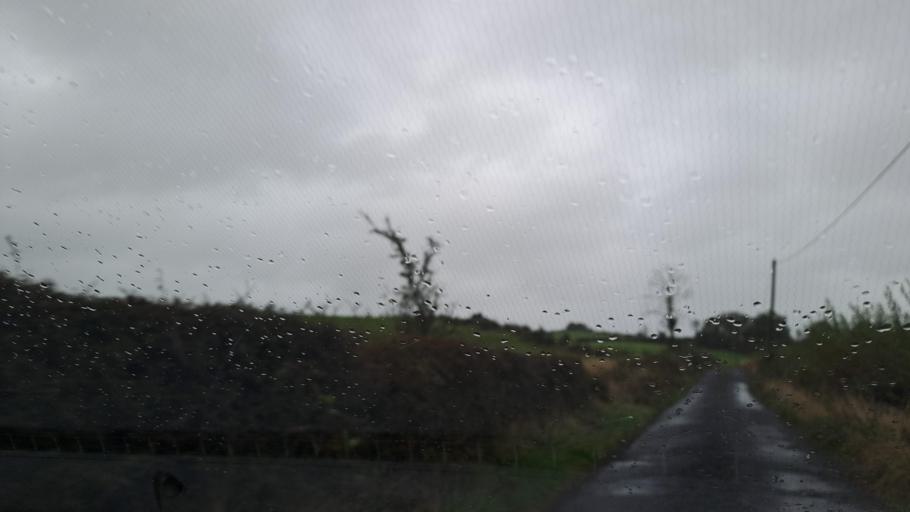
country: IE
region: Ulster
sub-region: An Cabhan
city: Kingscourt
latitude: 54.0069
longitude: -6.8360
